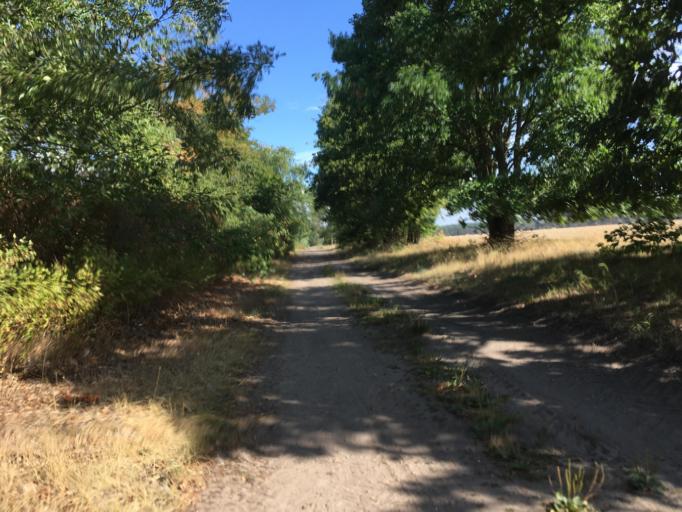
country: DE
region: Brandenburg
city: Zehdenick
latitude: 52.9562
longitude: 13.3819
